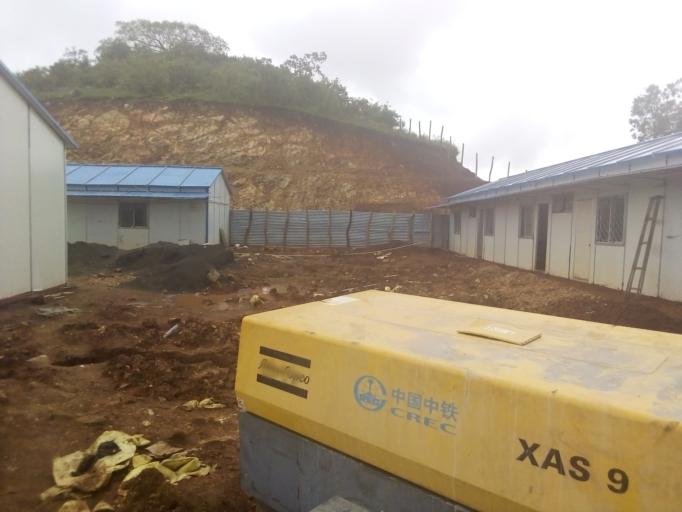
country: ET
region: Southern Nations, Nationalities, and People's Region
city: Areka
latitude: 7.2270
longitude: 37.2630
